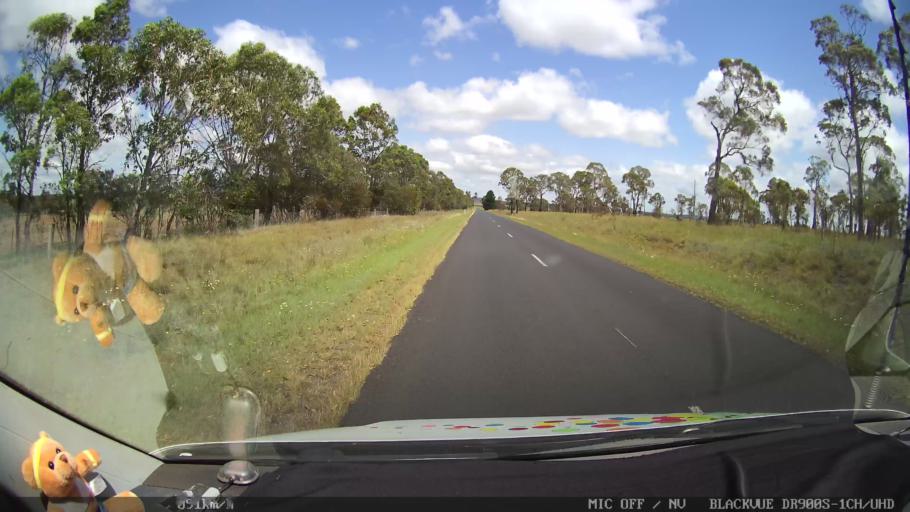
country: AU
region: New South Wales
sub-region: Glen Innes Severn
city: Glen Innes
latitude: -29.6879
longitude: 151.7060
